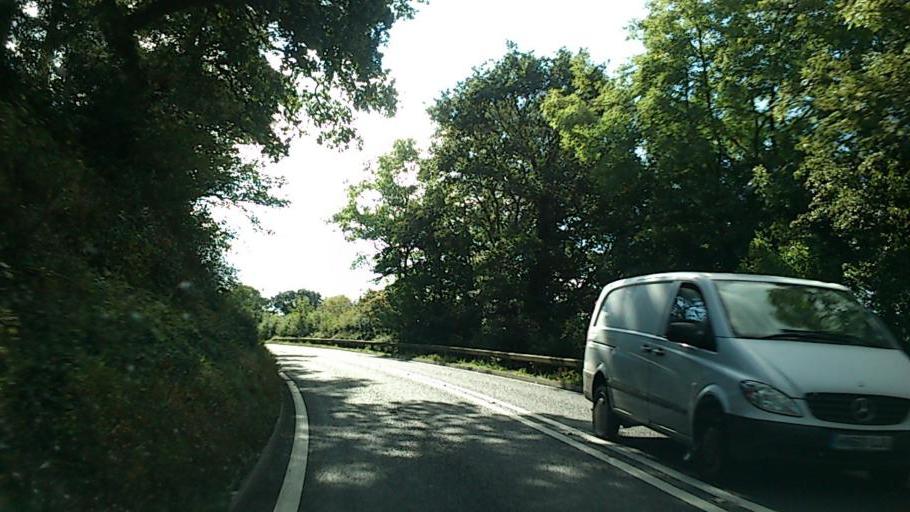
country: GB
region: Wales
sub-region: Sir Powys
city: Welshpool
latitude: 52.6827
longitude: -3.0913
